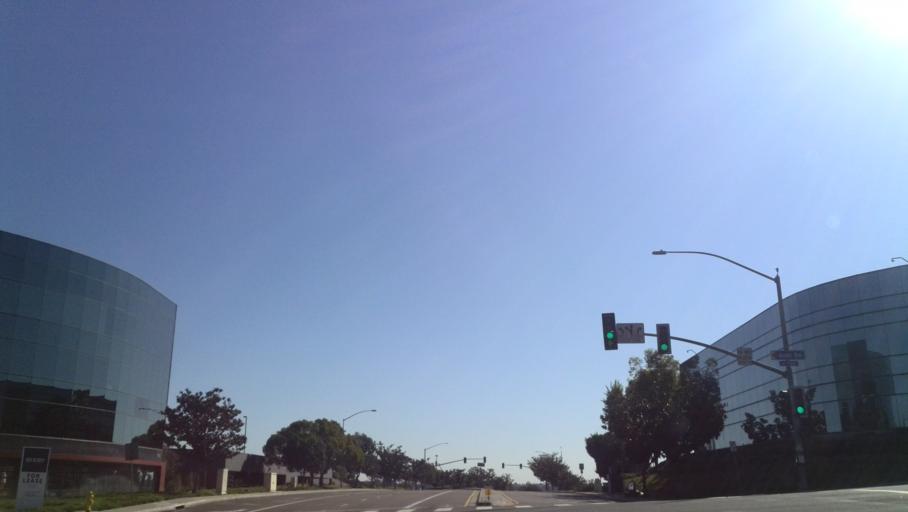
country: US
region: California
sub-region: San Diego County
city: San Diego
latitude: 32.8088
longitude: -117.1192
